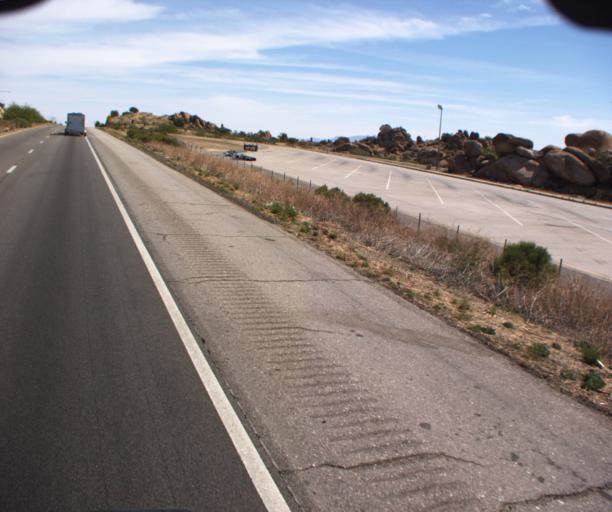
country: US
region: Arizona
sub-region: Cochise County
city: Saint David
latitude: 32.0603
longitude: -110.0769
